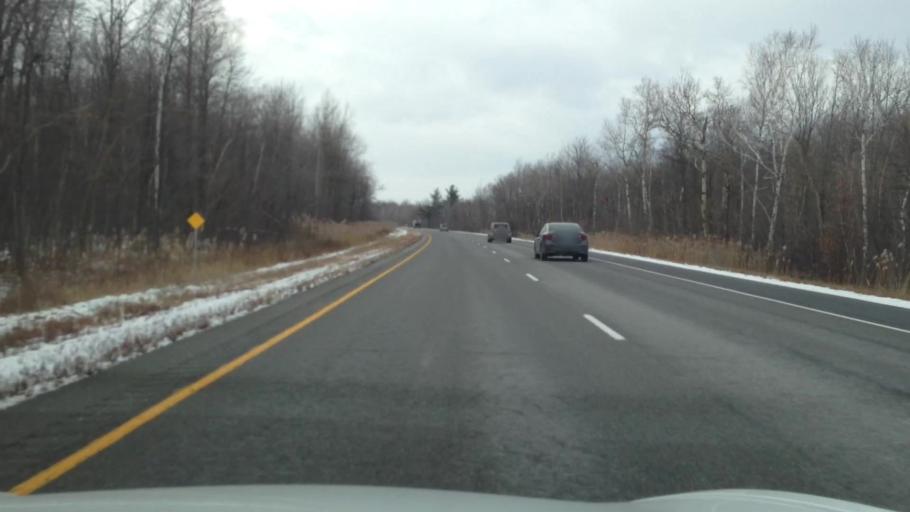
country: CA
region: Ontario
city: Casselman
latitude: 45.3059
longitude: -75.1089
